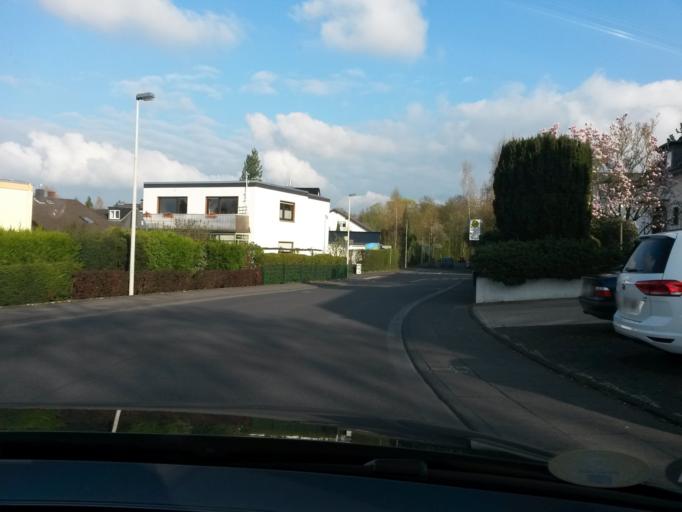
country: DE
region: North Rhine-Westphalia
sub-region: Regierungsbezirk Koln
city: Alfter
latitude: 50.7114
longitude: 7.0394
